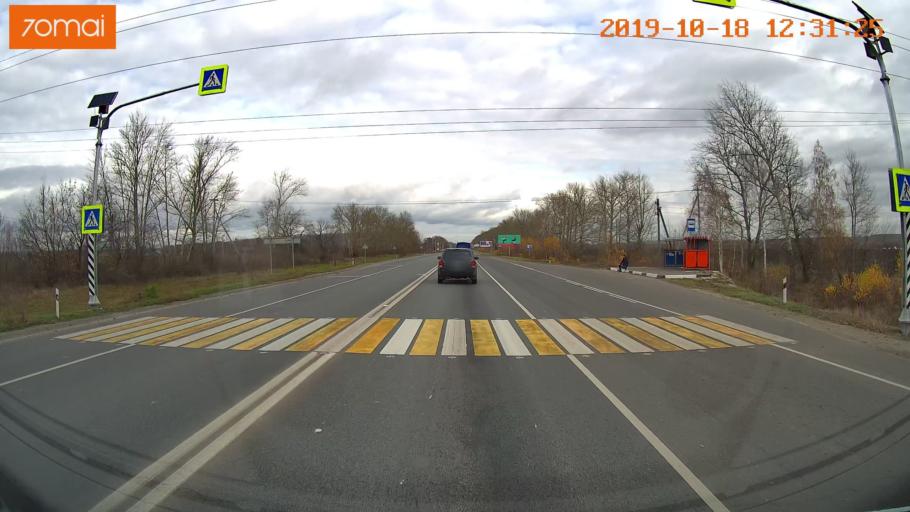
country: RU
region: Rjazan
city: Ryazan'
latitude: 54.5932
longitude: 39.6121
